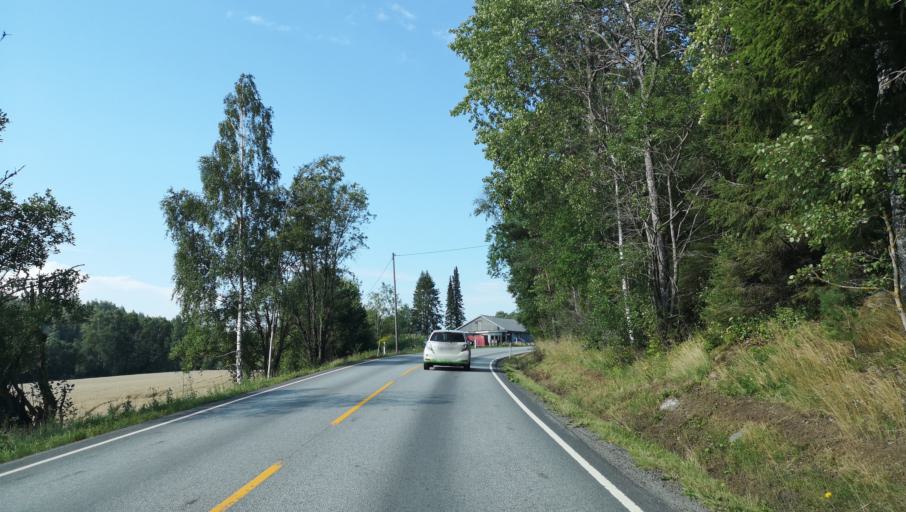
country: NO
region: Ostfold
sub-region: Valer
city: Kirkebygda
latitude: 59.5032
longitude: 10.8380
